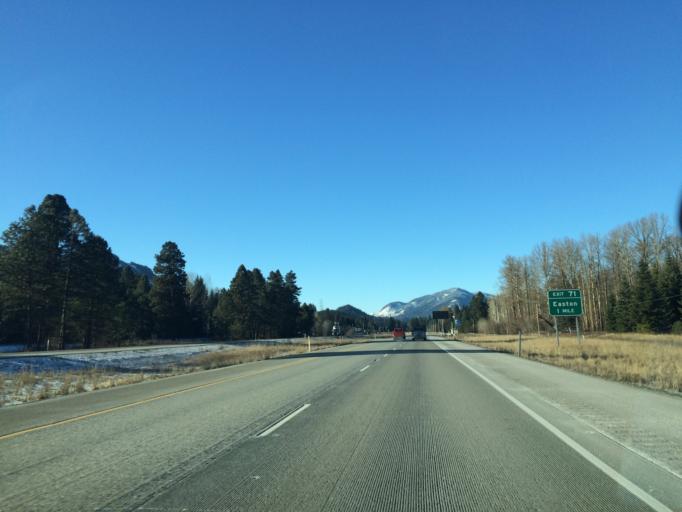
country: US
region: Washington
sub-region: Kittitas County
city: Cle Elum
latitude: 47.2238
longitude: -121.1546
